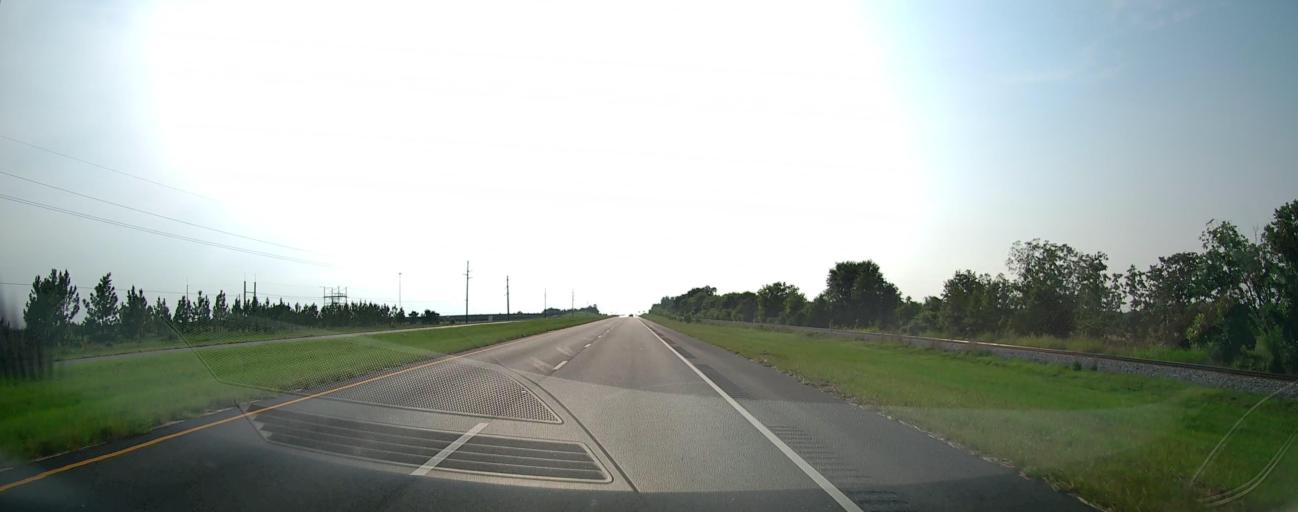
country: US
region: Georgia
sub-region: Taylor County
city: Butler
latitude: 32.5772
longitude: -84.3096
